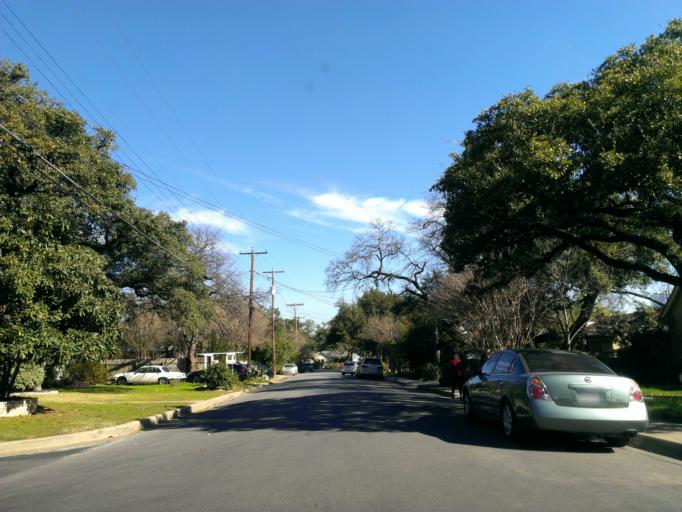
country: US
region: Texas
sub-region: Travis County
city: Austin
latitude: 30.2603
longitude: -97.7631
